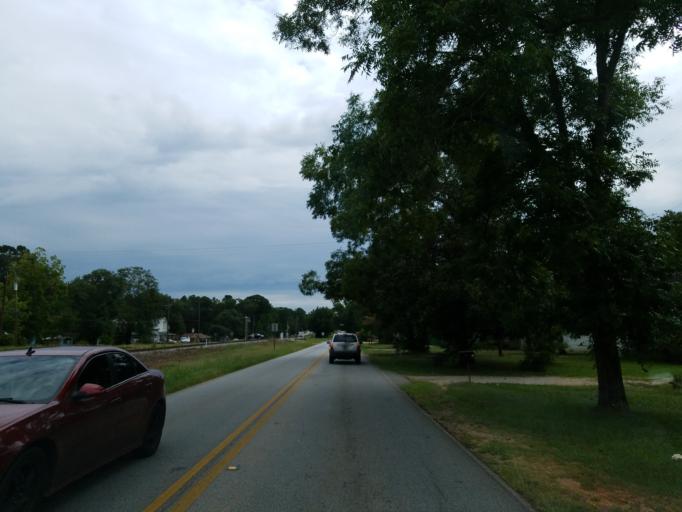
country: US
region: Georgia
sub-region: Spalding County
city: Experiment
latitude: 33.2969
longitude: -84.2865
